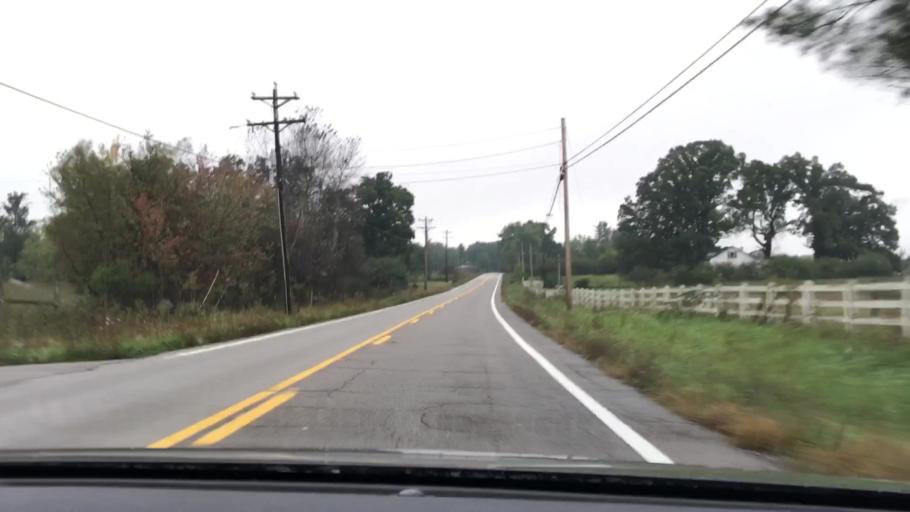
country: US
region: Tennessee
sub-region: Fentress County
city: Grimsley
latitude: 36.1996
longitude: -85.0198
